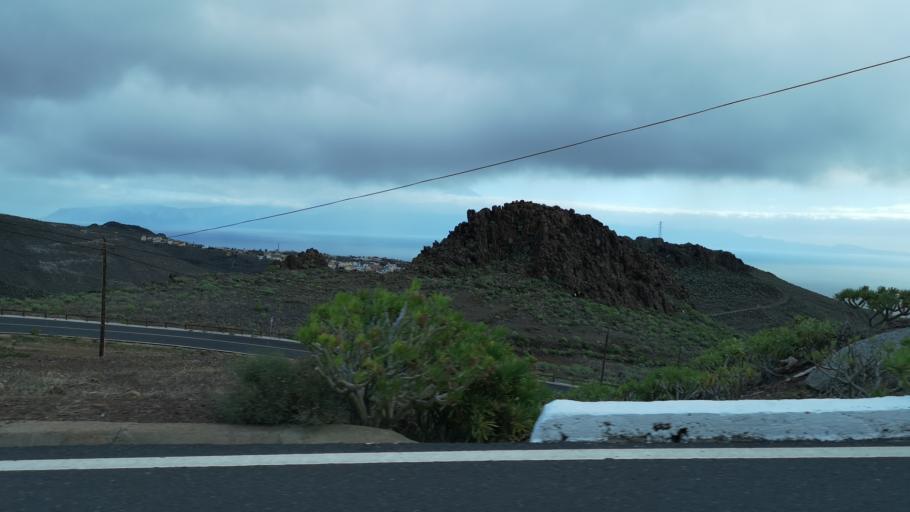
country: ES
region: Canary Islands
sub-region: Provincia de Santa Cruz de Tenerife
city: San Sebastian de la Gomera
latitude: 28.0835
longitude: -17.1296
